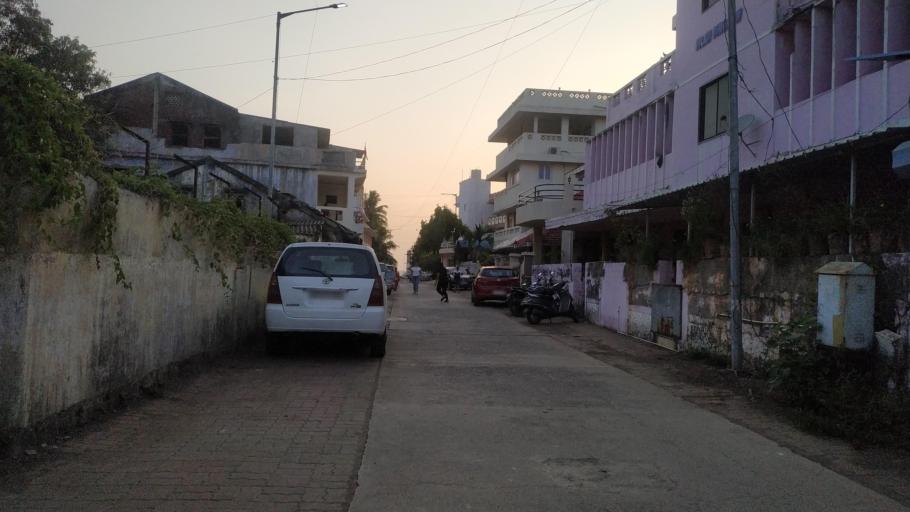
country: IN
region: Daman and Diu
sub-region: Daman District
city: Daman
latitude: 20.4147
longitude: 72.8318
